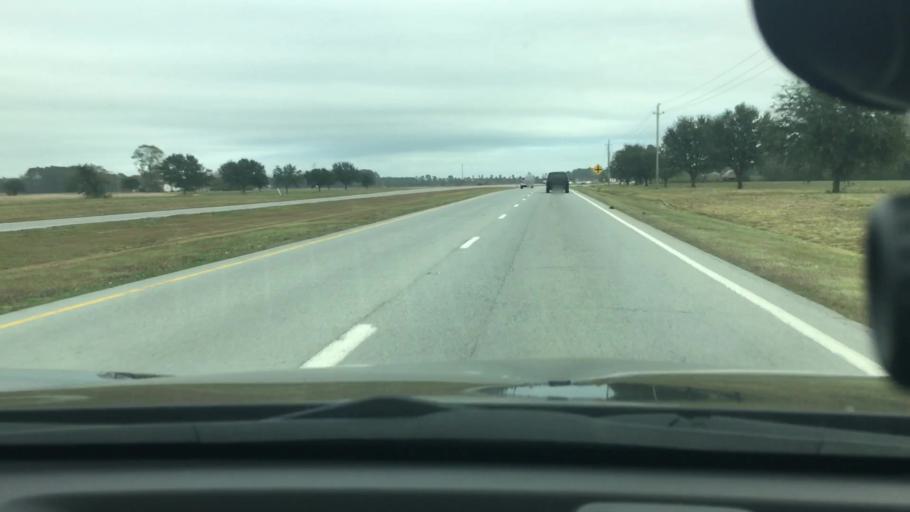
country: US
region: North Carolina
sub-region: Pitt County
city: Greenville
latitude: 35.6255
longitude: -77.2727
